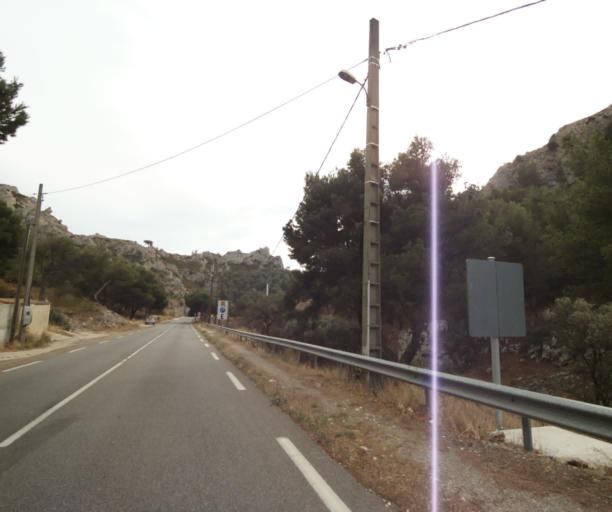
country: FR
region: Provence-Alpes-Cote d'Azur
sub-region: Departement des Bouches-du-Rhone
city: Le Rove
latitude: 43.3583
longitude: 5.2758
